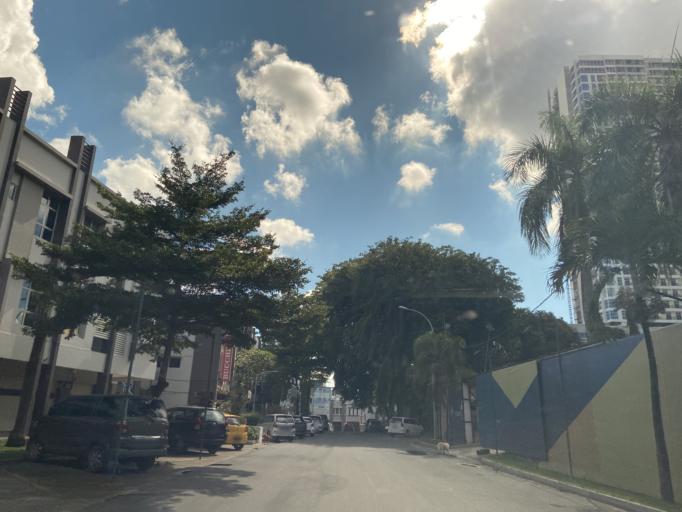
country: SG
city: Singapore
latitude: 1.1438
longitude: 104.0080
